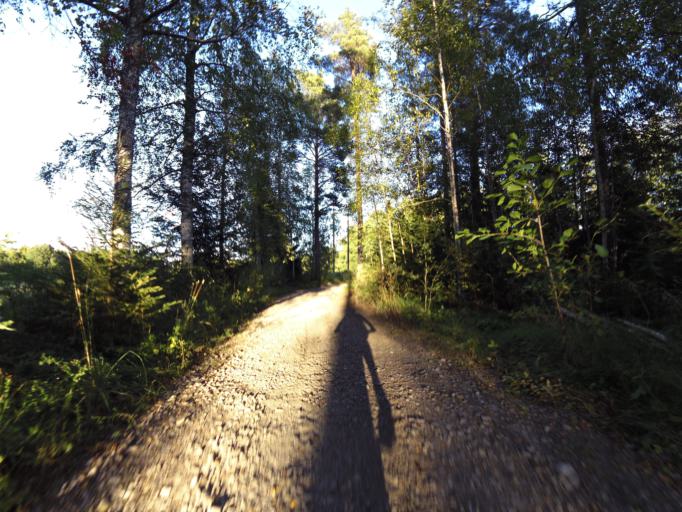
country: SE
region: Gaevleborg
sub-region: Gavle Kommun
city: Gavle
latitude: 60.7219
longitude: 17.1433
